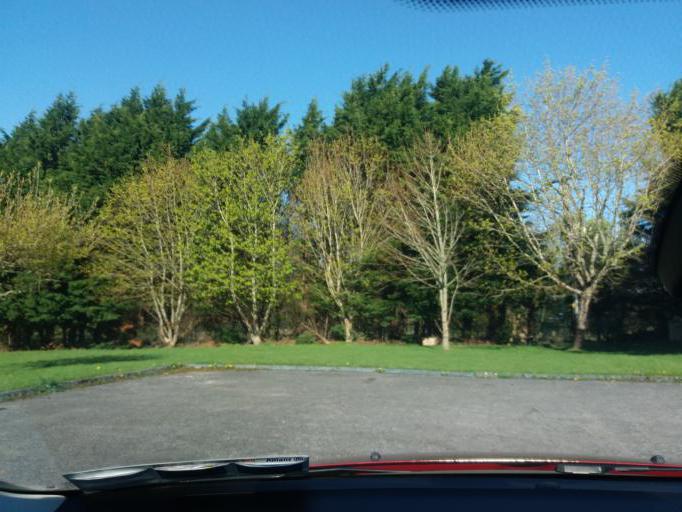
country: IE
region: Munster
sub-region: Ciarrai
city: Cill Airne
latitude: 52.0517
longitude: -9.5189
